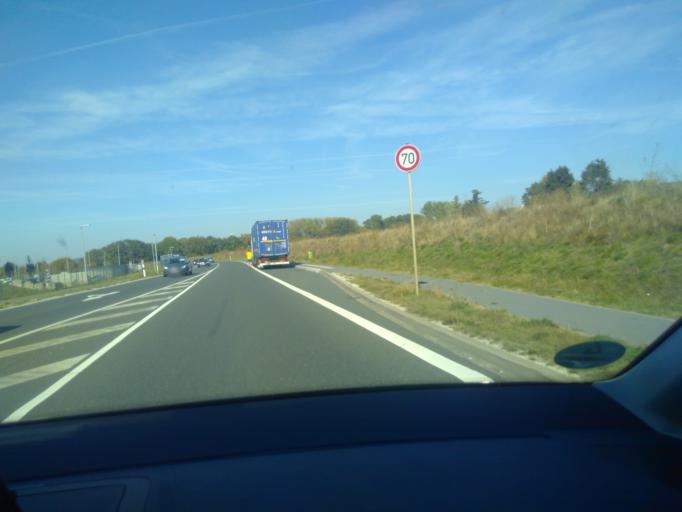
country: DE
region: North Rhine-Westphalia
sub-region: Regierungsbezirk Detmold
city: Steinhagen
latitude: 52.0283
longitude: 8.3802
